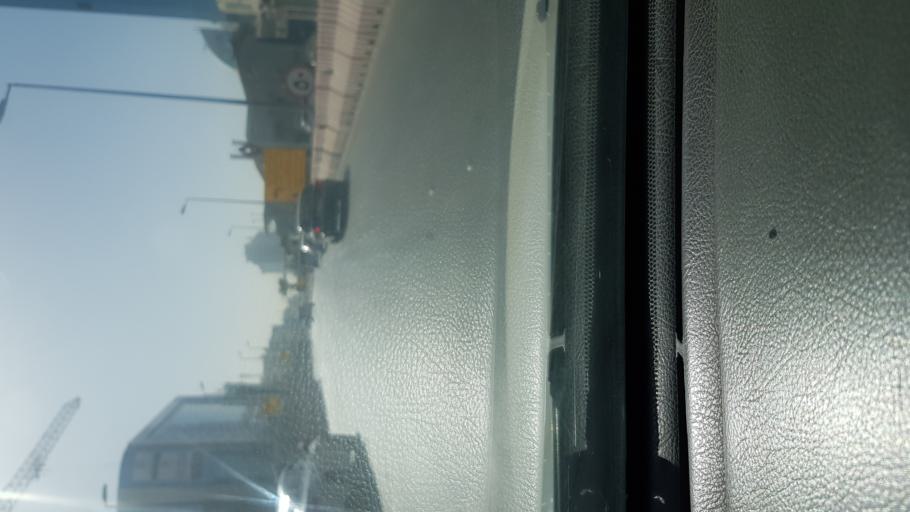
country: SA
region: Ar Riyad
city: Riyadh
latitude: 24.7148
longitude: 46.6751
